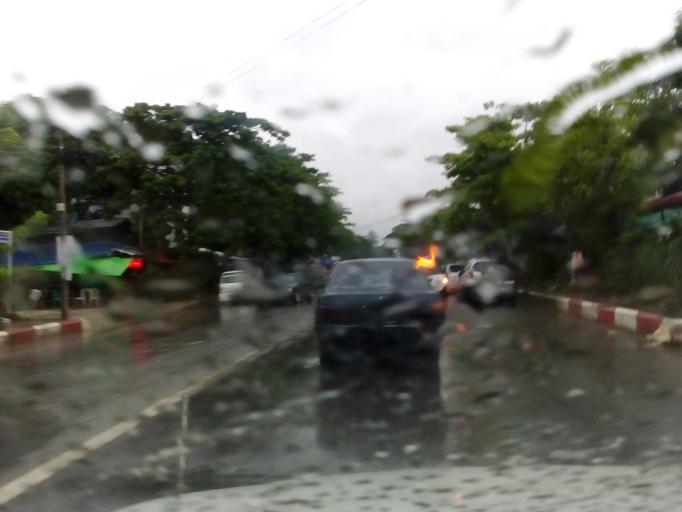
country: MM
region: Yangon
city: Yangon
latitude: 16.8241
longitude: 96.1647
